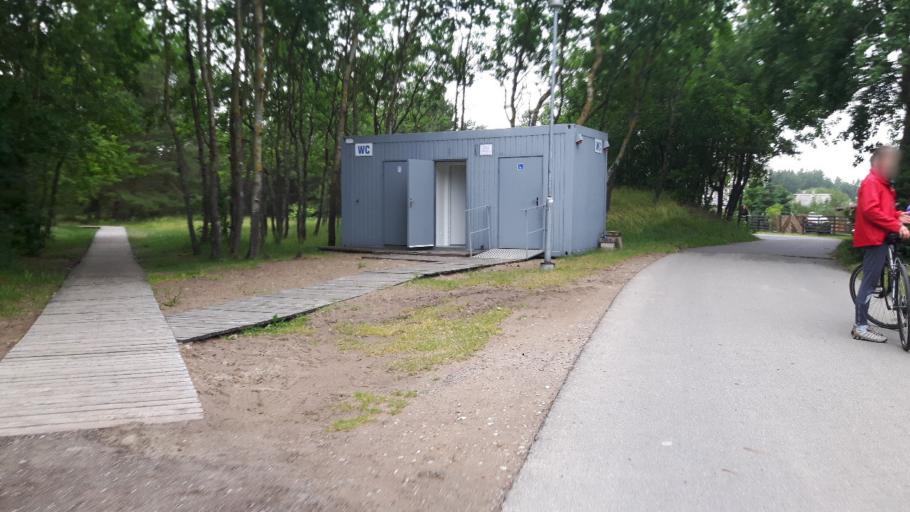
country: LT
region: Klaipedos apskritis
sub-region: Palanga
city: Sventoji
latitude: 56.0145
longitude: 21.0766
